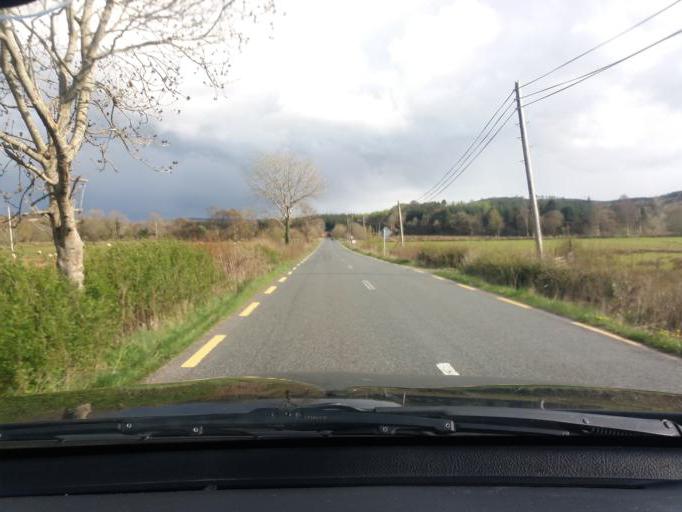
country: IE
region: Connaught
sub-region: County Leitrim
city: Manorhamilton
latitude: 54.3356
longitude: -8.2198
